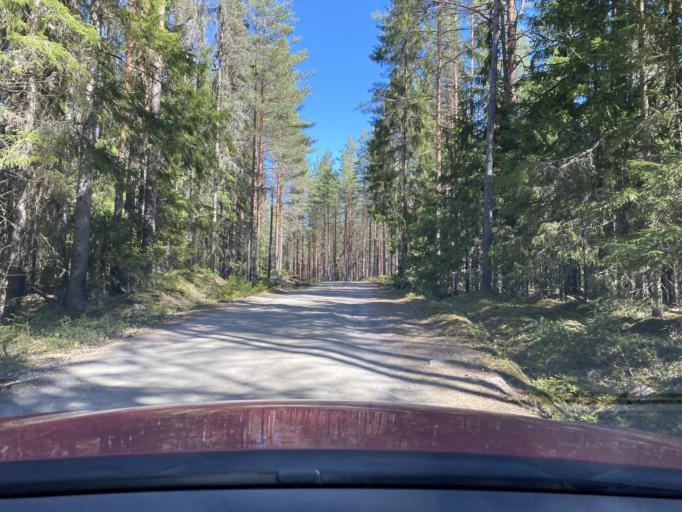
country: FI
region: Uusimaa
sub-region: Helsinki
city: Kaerkoelae
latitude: 60.6610
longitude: 23.8580
